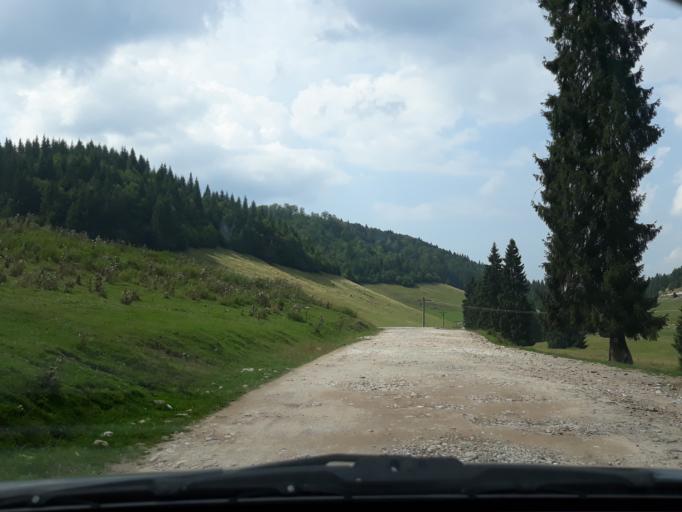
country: RO
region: Alba
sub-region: Comuna Arieseni
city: Arieseni
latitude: 46.5870
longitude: 22.6934
